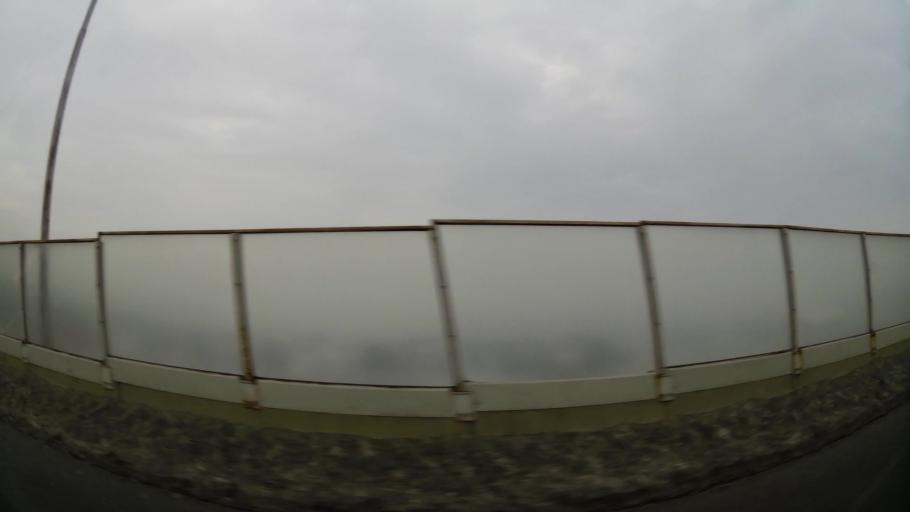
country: MK
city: Kondovo
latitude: 42.0509
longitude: 21.3387
